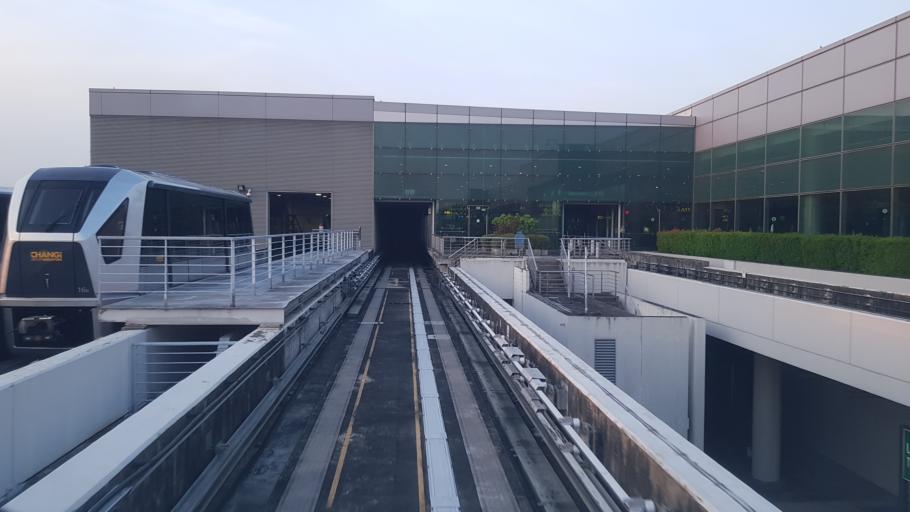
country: SG
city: Singapore
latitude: 1.3507
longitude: 103.9841
